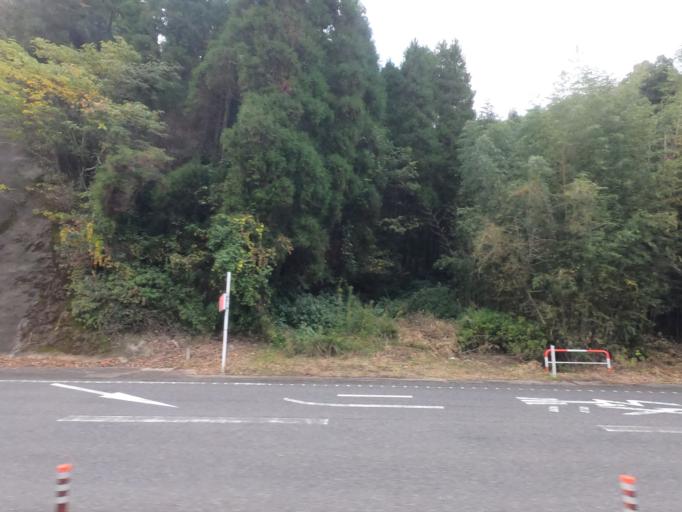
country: JP
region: Kumamoto
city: Minamata
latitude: 32.2442
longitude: 130.4850
